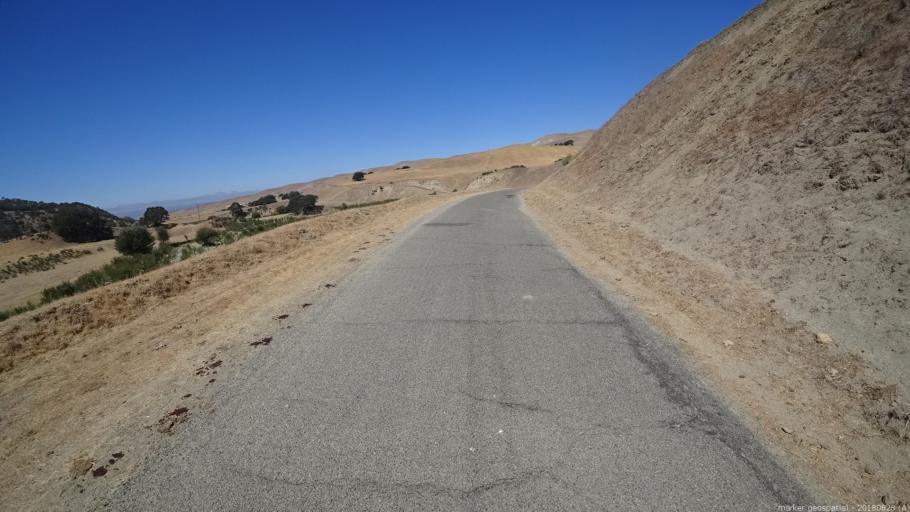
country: US
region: California
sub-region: San Luis Obispo County
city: San Miguel
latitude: 36.0677
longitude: -120.7729
